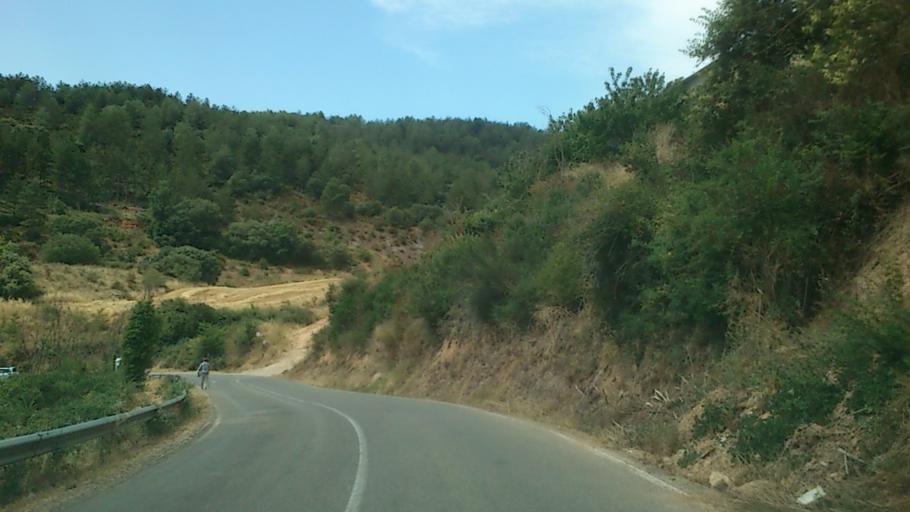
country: ES
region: Castille and Leon
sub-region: Provincia de Burgos
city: Frias
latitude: 42.7608
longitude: -3.2976
